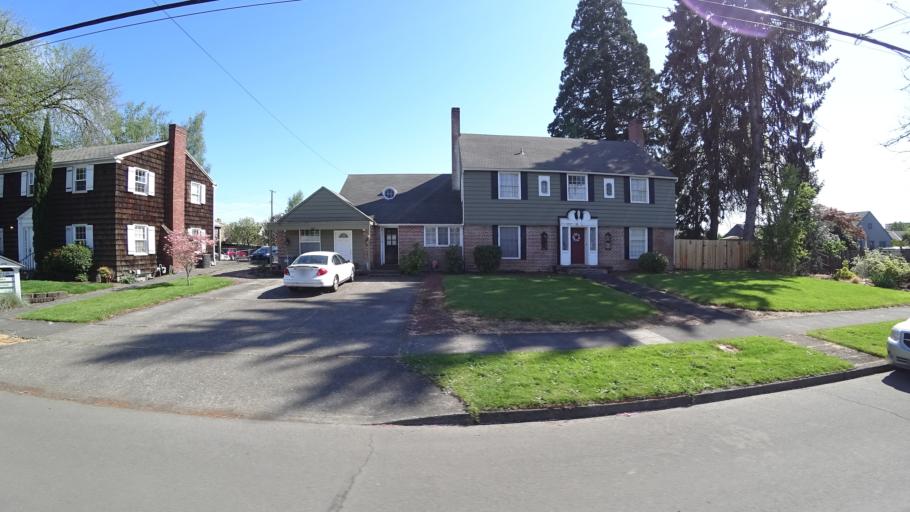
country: US
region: Oregon
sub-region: Washington County
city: Hillsboro
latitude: 45.5238
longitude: -122.9835
